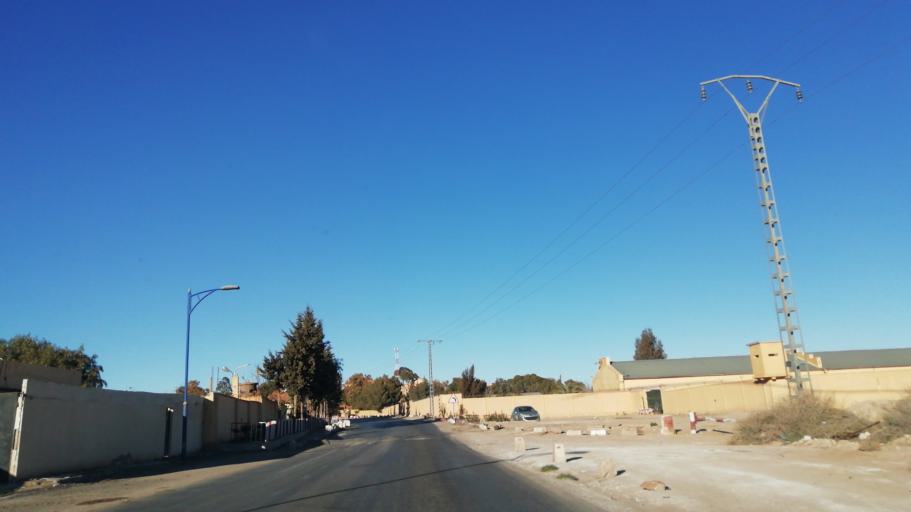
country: DZ
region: Saida
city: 'Ain el Hadjar
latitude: 34.1427
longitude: 0.0713
